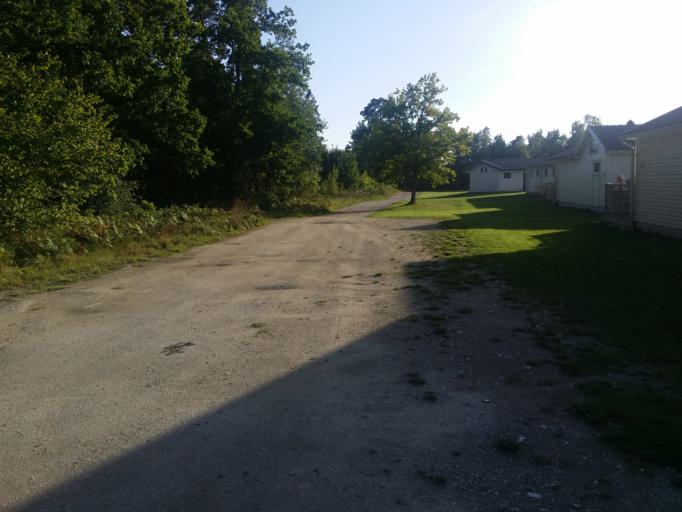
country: SE
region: Gotland
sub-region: Gotland
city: Klintehamn
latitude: 57.4851
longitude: 18.1410
